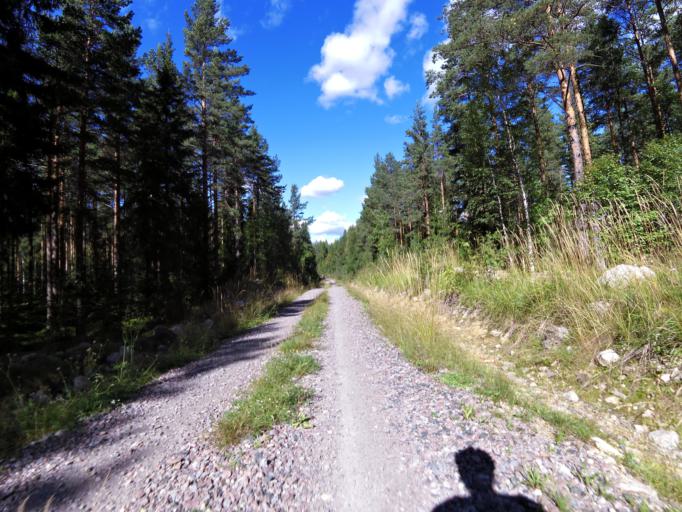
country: SE
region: Gaevleborg
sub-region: Gavle Kommun
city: Valbo
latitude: 60.7273
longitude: 16.9999
